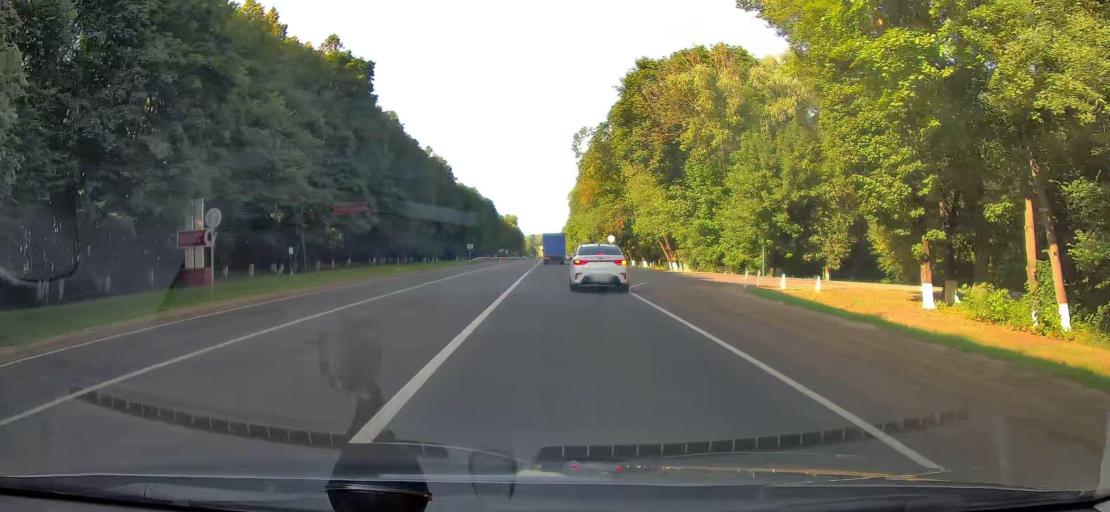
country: RU
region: Orjol
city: Mtsensk
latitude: 53.1646
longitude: 36.3838
